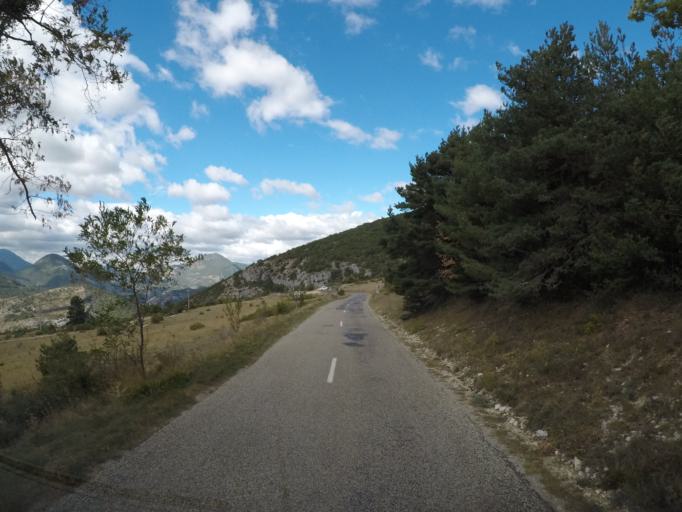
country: FR
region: Provence-Alpes-Cote d'Azur
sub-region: Departement du Vaucluse
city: Sault
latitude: 44.1529
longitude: 5.4481
